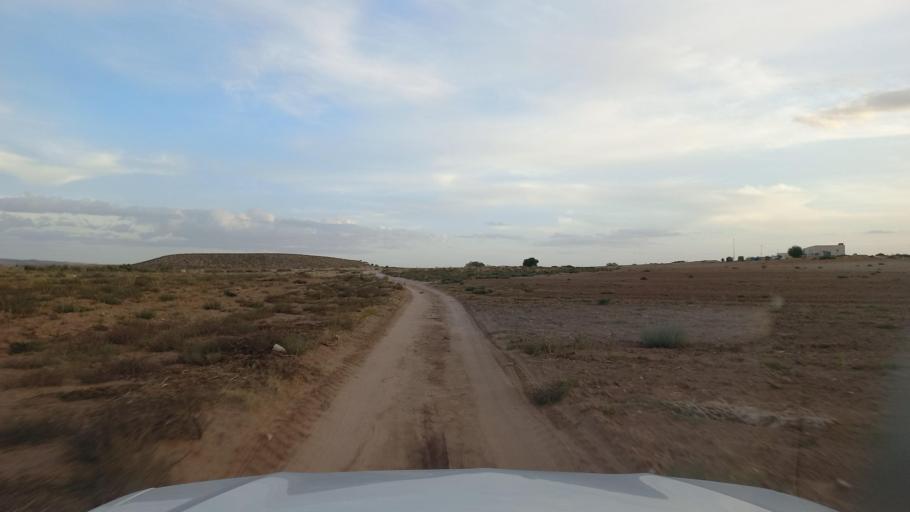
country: TN
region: Al Qasrayn
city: Sbiba
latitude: 35.4080
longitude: 9.0887
